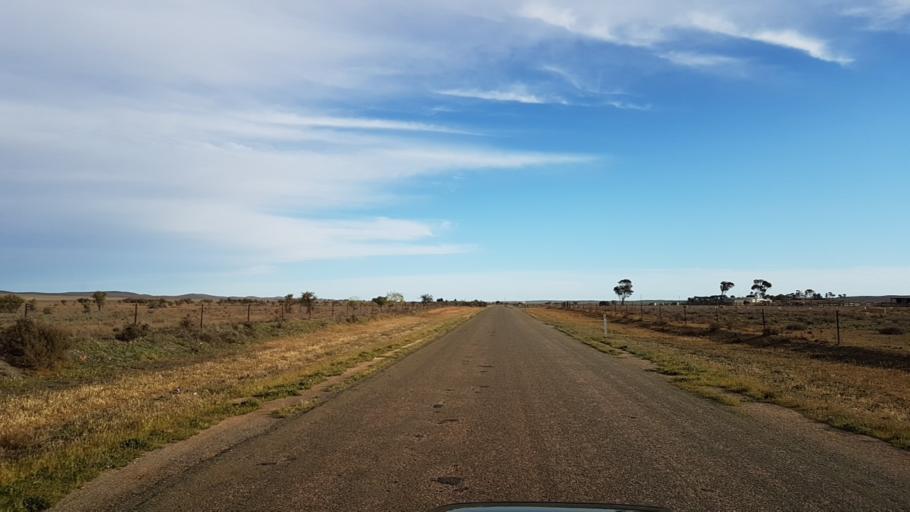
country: AU
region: South Australia
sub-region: Peterborough
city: Peterborough
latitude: -32.9844
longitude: 138.8508
